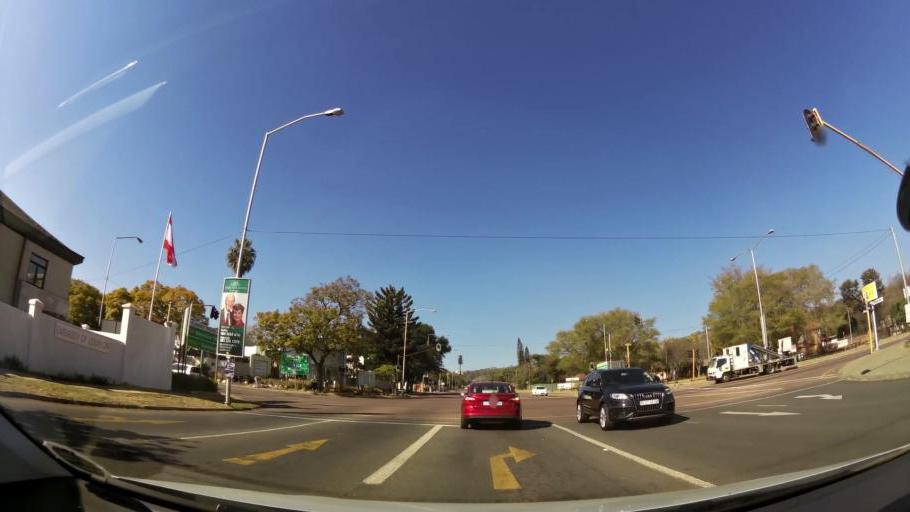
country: ZA
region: Gauteng
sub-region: City of Tshwane Metropolitan Municipality
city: Pretoria
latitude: -25.7735
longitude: 28.2245
